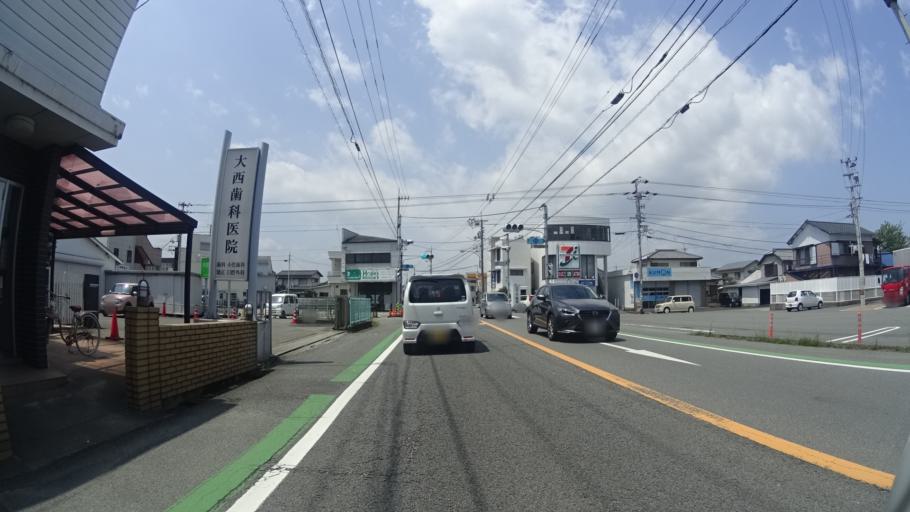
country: JP
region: Tokushima
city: Ishii
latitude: 34.0720
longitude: 134.4829
